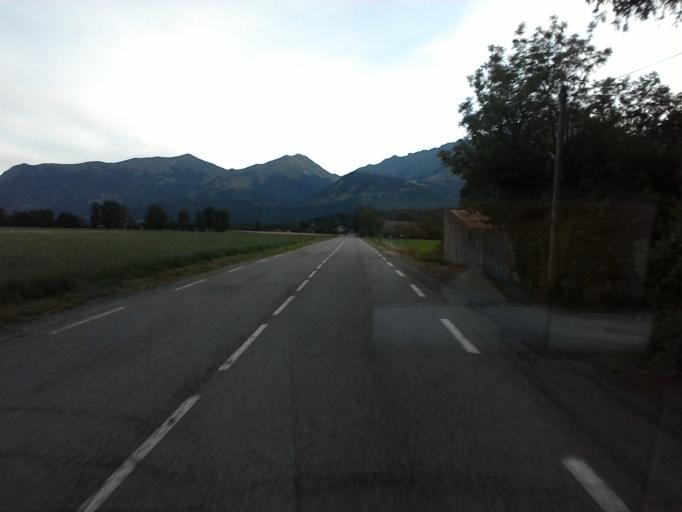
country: FR
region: Provence-Alpes-Cote d'Azur
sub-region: Departement des Hautes-Alpes
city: Saint-Bonnet-en-Champsaur
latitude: 44.7451
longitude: 6.0078
